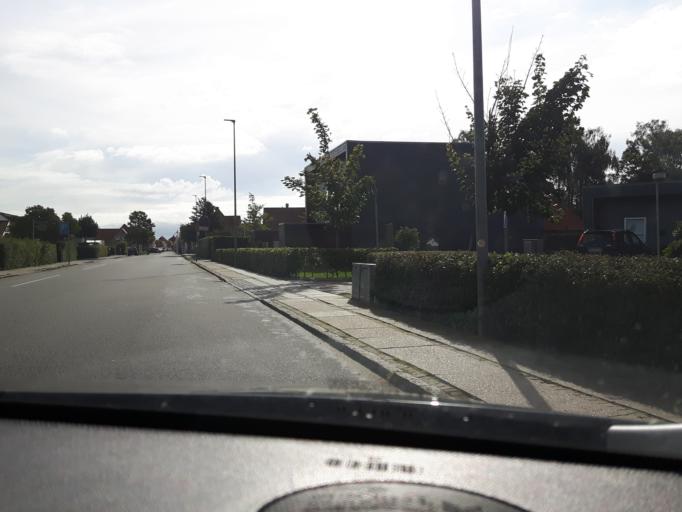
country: DK
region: Central Jutland
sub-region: Hedensted Kommune
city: Juelsminde
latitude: 55.7156
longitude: 10.0065
